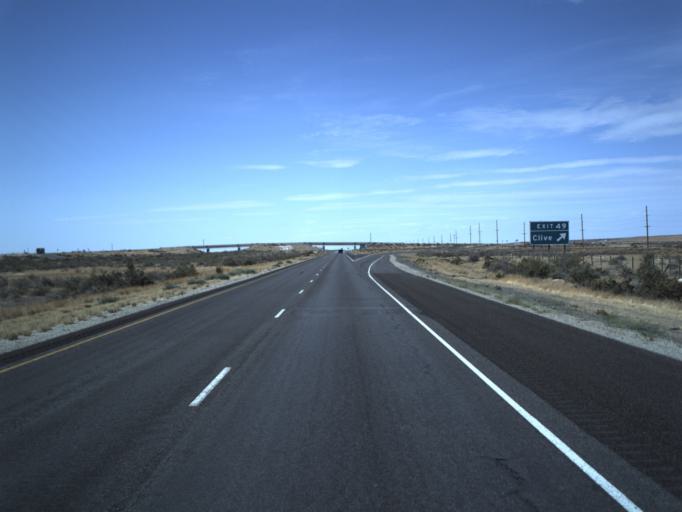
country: US
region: Utah
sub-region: Tooele County
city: Grantsville
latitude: 40.7346
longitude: -113.1059
